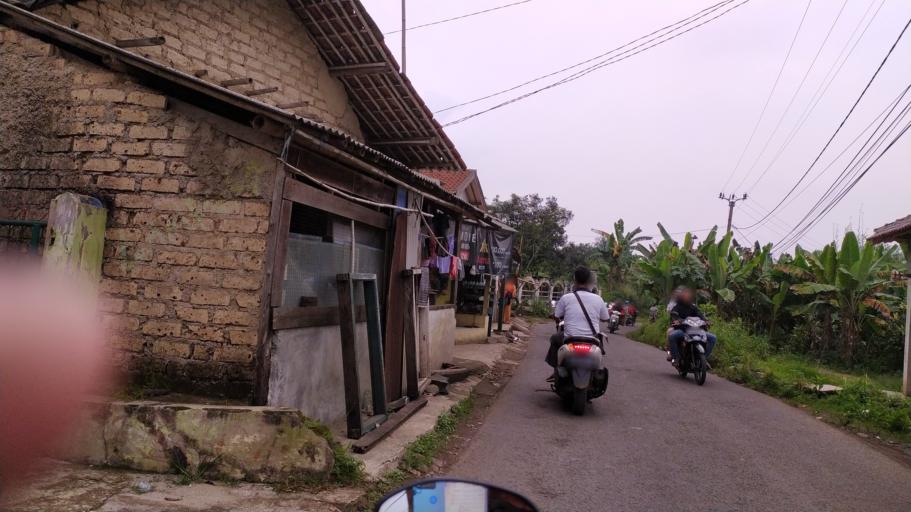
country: ID
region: West Java
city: Ciampea
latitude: -6.5851
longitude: 106.7059
